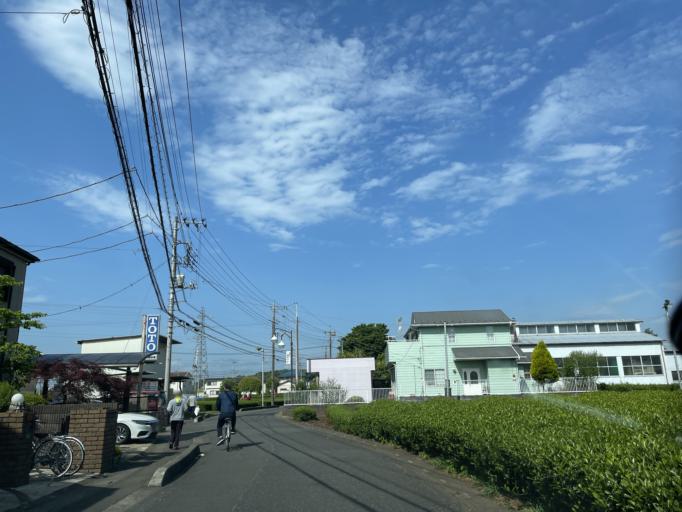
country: JP
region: Saitama
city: Sayama
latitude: 35.8107
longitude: 139.3946
